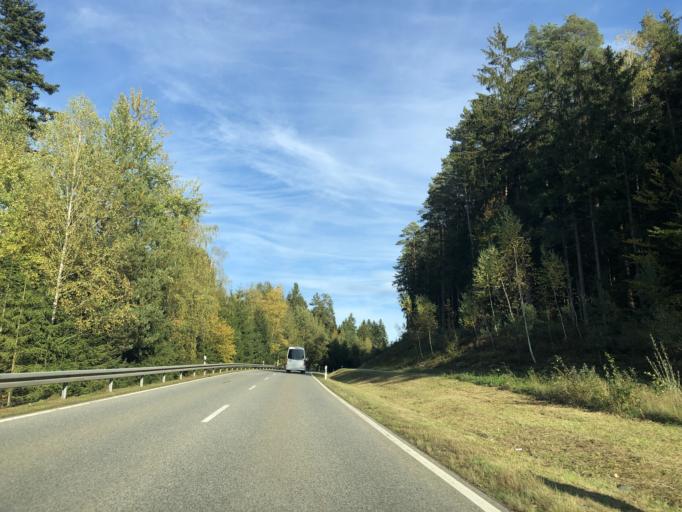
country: DE
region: Bavaria
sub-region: Lower Bavaria
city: Teisnach
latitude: 49.0463
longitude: 13.0094
